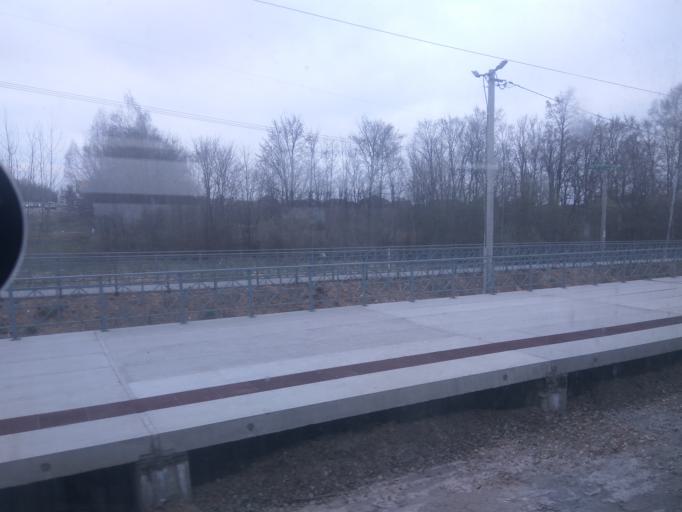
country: RU
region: Moskovskaya
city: Sergiyev Posad
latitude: 56.3437
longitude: 38.1246
